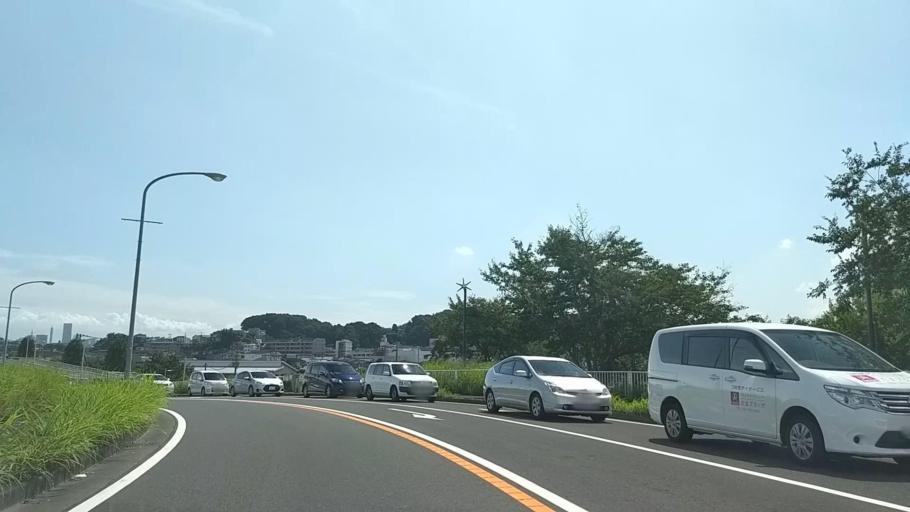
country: JP
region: Kanagawa
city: Yokohama
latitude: 35.5122
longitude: 139.6002
